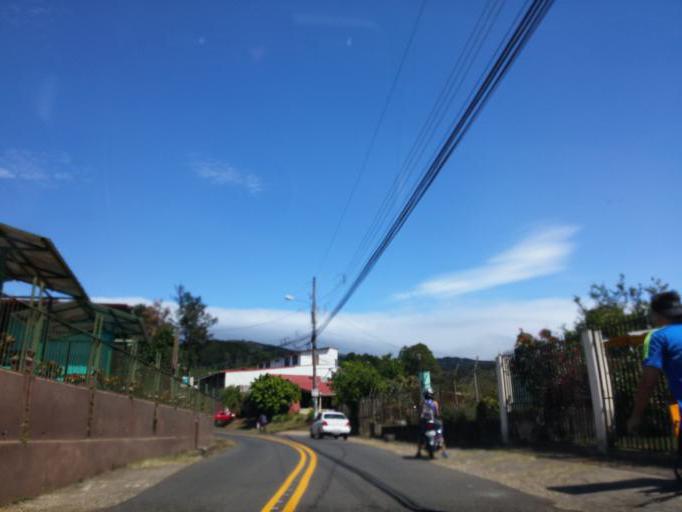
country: CR
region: Heredia
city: Santo Domingo
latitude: 10.0583
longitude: -84.1354
